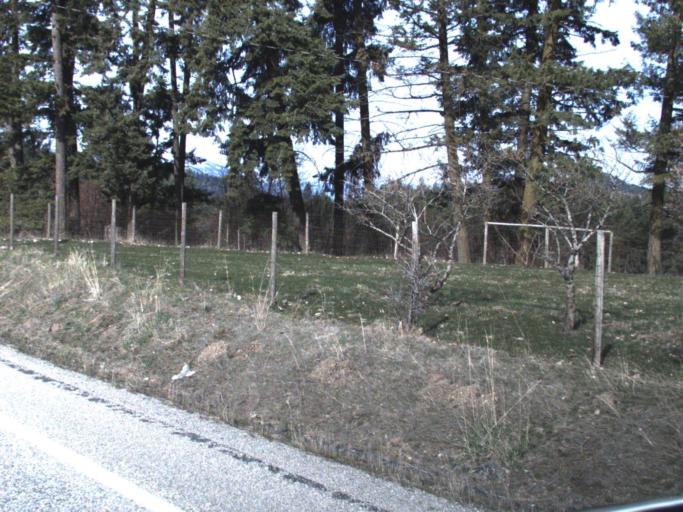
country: US
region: Washington
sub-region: Stevens County
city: Colville
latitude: 48.5154
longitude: -117.7968
